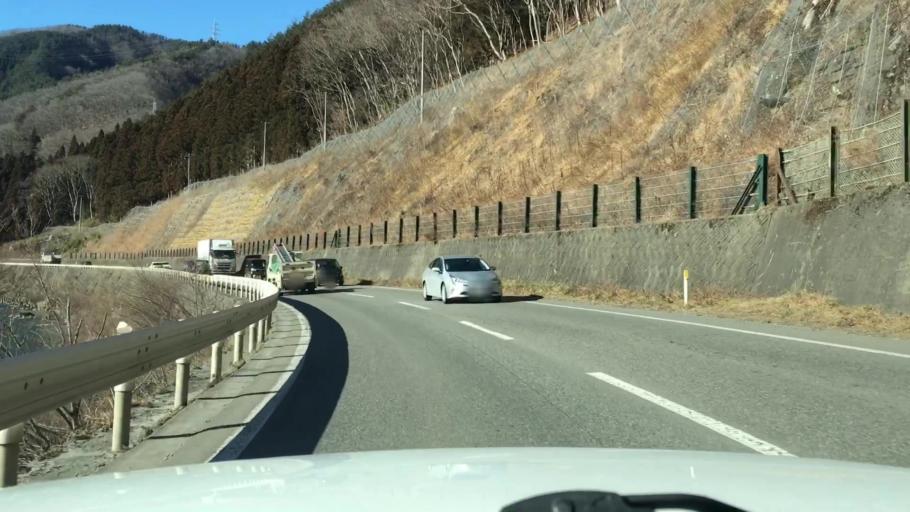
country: JP
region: Iwate
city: Miyako
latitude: 39.6267
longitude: 141.8235
